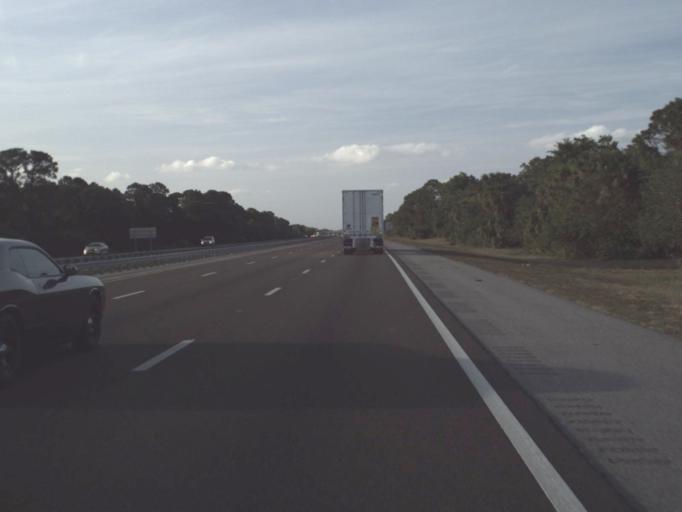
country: US
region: Florida
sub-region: Brevard County
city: Port Saint John
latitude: 28.4338
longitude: -80.8202
